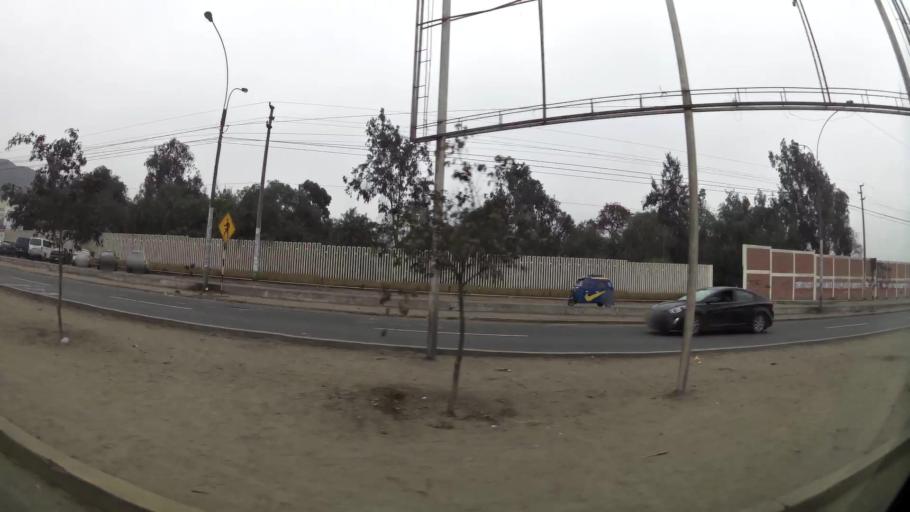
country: PE
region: Lima
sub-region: Lima
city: Urb. Santo Domingo
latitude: -11.9144
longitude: -77.0401
